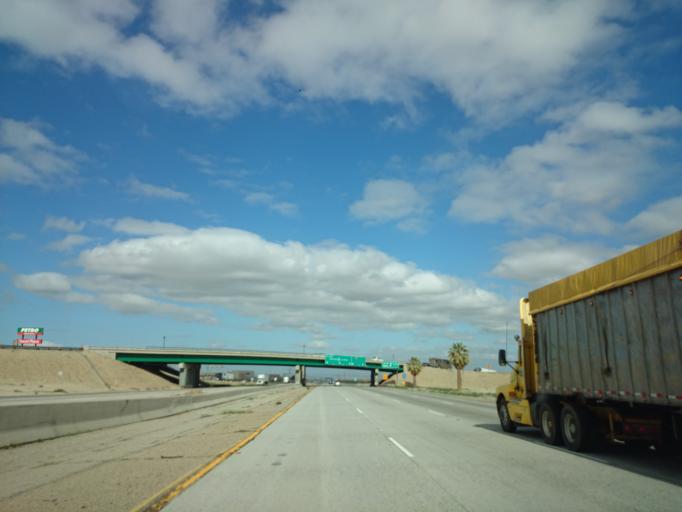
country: US
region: California
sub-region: Kern County
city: Frazier Park
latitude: 34.9849
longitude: -118.9448
